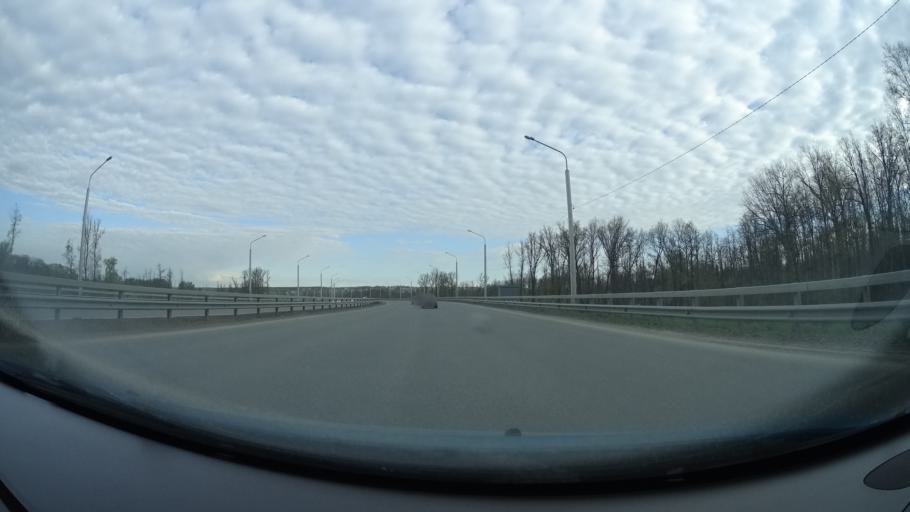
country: RU
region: Bashkortostan
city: Mikhaylovka
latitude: 54.7921
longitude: 55.9050
